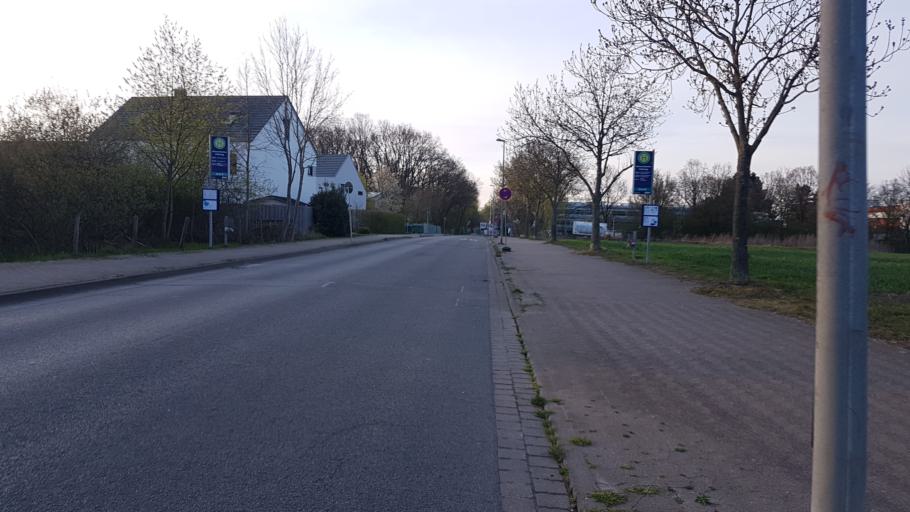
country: DE
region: Lower Saxony
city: Isernhagen Farster Bauerschaft
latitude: 52.4375
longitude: 9.8551
